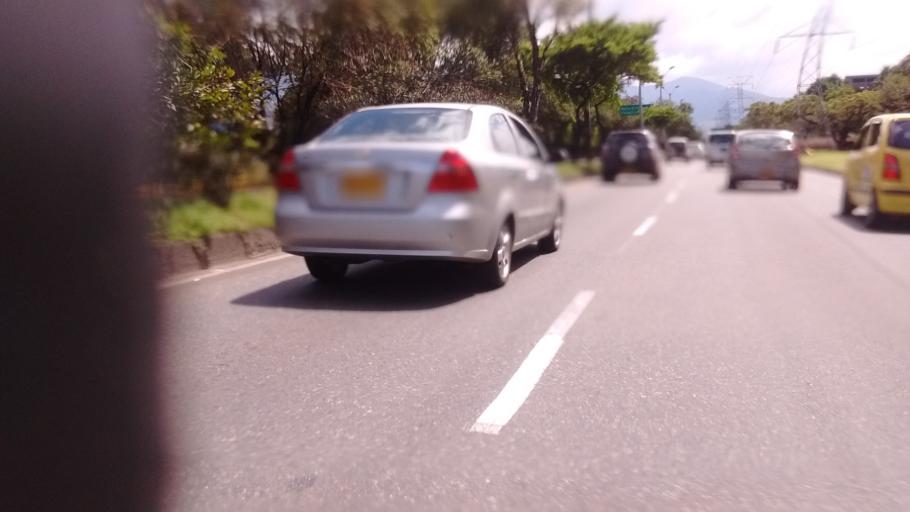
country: CO
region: Antioquia
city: Medellin
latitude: 6.2188
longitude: -75.5777
